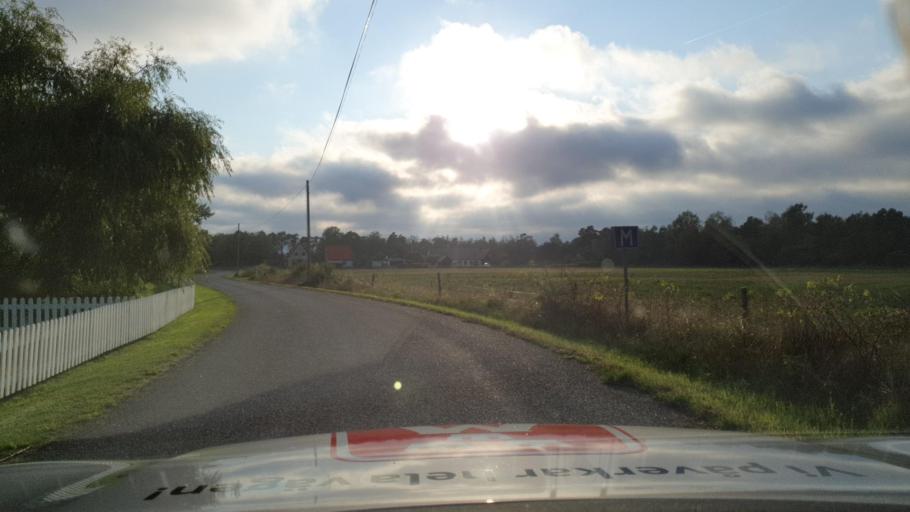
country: SE
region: Gotland
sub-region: Gotland
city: Klintehamn
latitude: 57.4442
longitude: 18.1600
